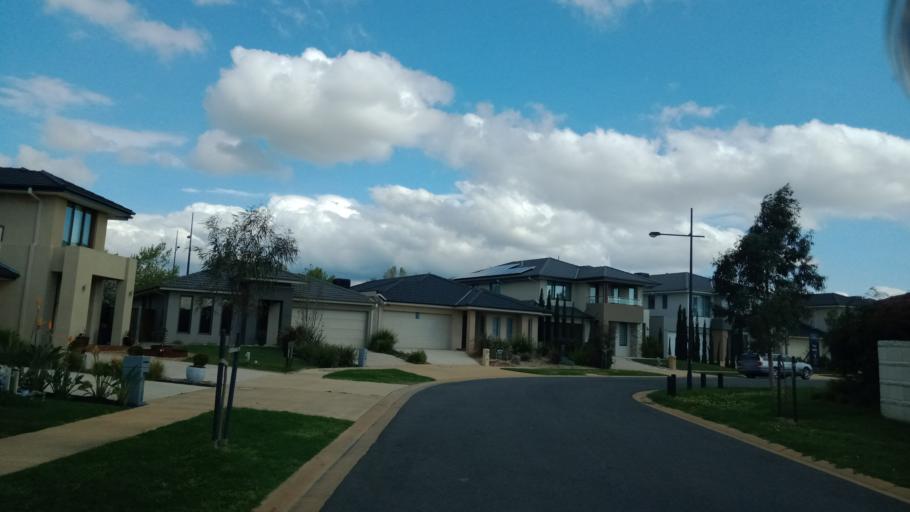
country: AU
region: Victoria
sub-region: Frankston
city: Sandhurst
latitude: -38.0798
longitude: 145.2094
